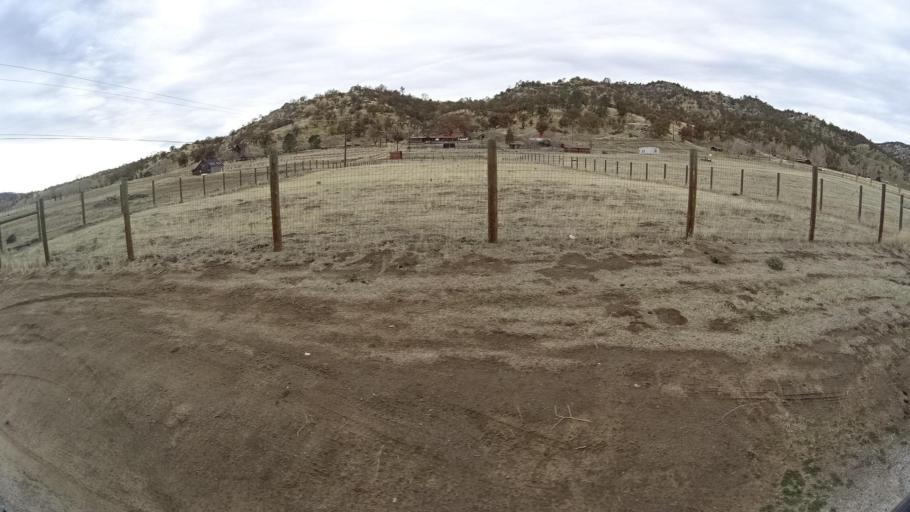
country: US
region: California
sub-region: Kern County
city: Stallion Springs
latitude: 35.1092
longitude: -118.6286
